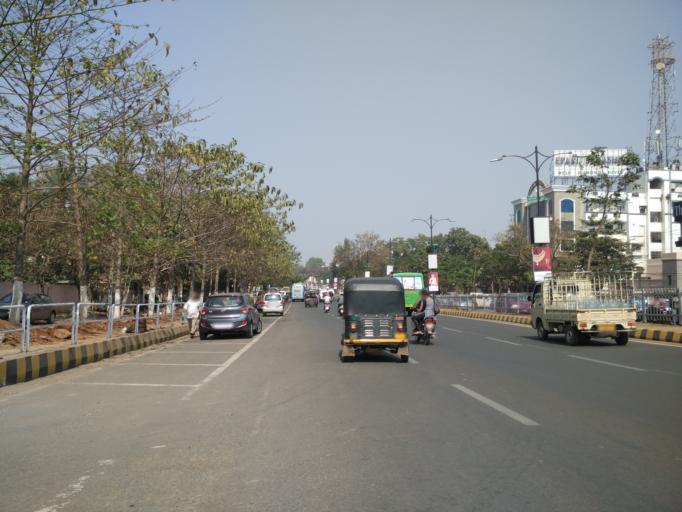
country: IN
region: Odisha
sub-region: Khordha
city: Bhubaneshwar
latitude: 20.2725
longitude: 85.8423
